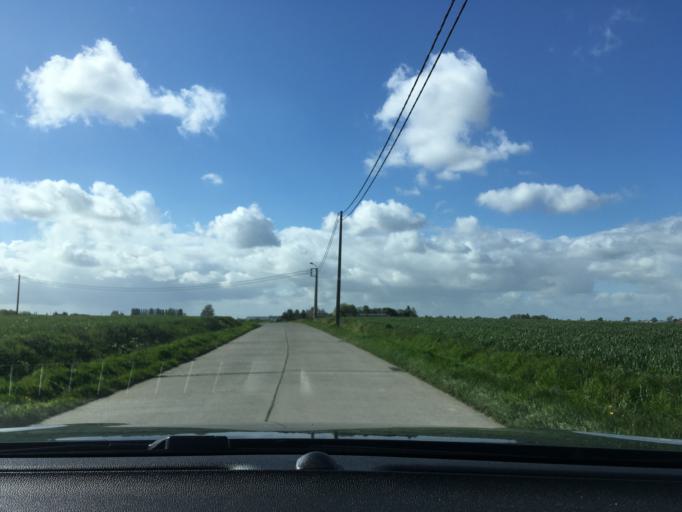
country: BE
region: Flanders
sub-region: Provincie West-Vlaanderen
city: Hooglede
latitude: 50.9985
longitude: 3.0871
